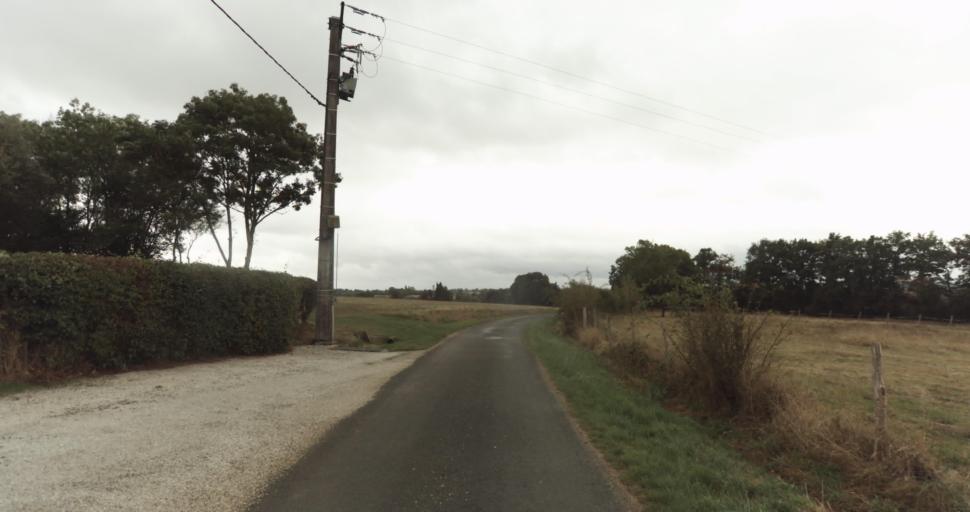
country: FR
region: Lower Normandy
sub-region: Departement de l'Orne
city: Sainte-Gauburge-Sainte-Colombe
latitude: 48.7362
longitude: 0.4763
